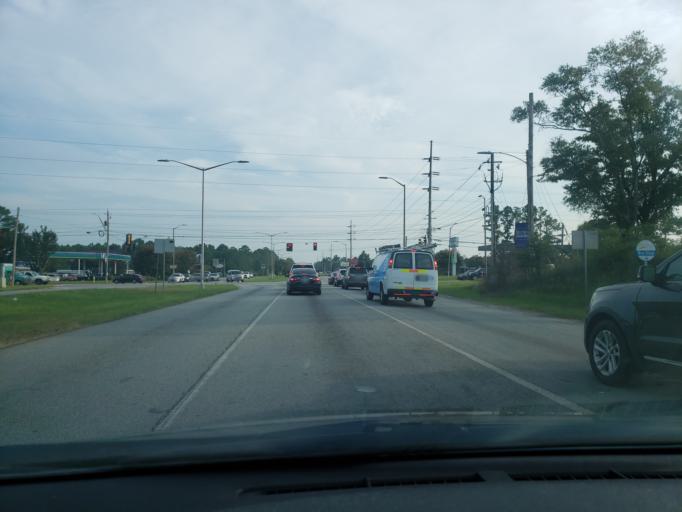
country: US
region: Georgia
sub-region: Dougherty County
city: Albany
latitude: 31.5850
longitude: -84.2193
